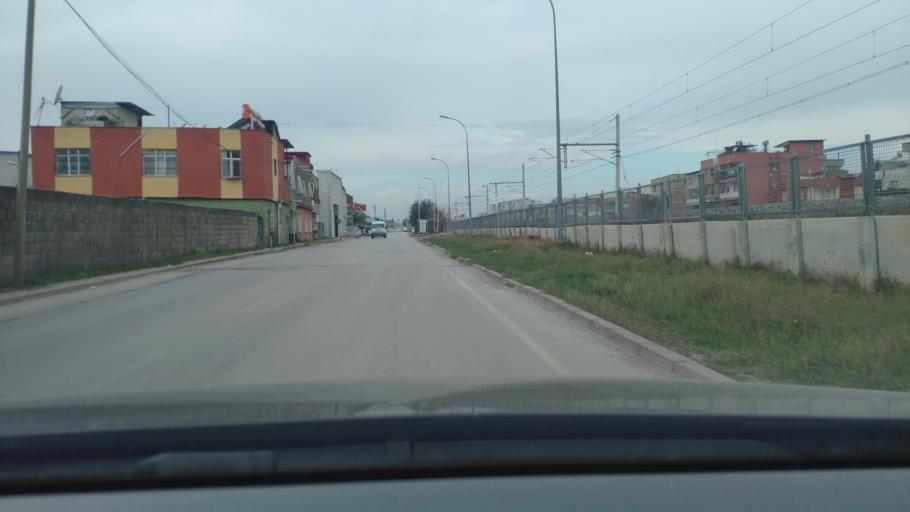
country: TR
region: Adana
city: Seyhan
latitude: 36.9977
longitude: 35.2692
